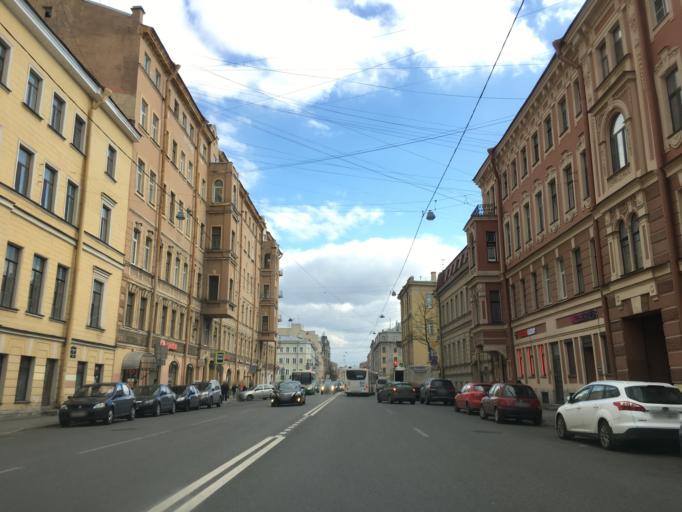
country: RU
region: St.-Petersburg
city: Admiralteisky
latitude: 59.9219
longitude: 30.2860
